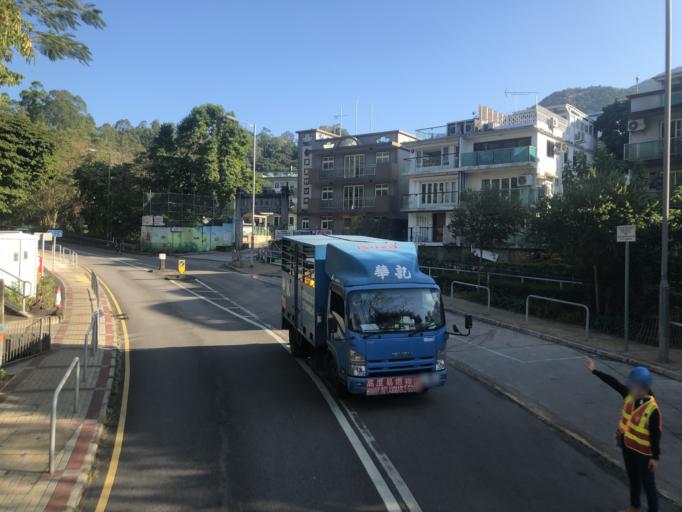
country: HK
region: Sai Kung
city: Sai Kung
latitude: 22.3515
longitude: 114.2518
